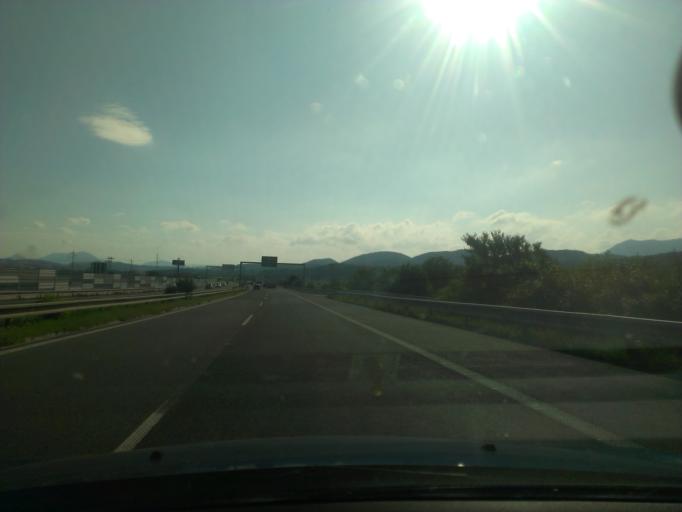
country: SK
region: Nitriansky
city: Puchov
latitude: 49.0463
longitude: 18.3066
